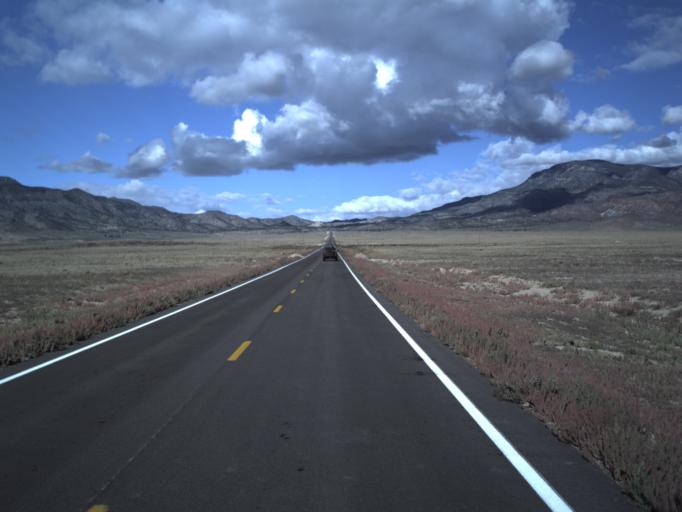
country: US
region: Utah
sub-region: Beaver County
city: Milford
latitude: 38.4824
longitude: -113.4436
